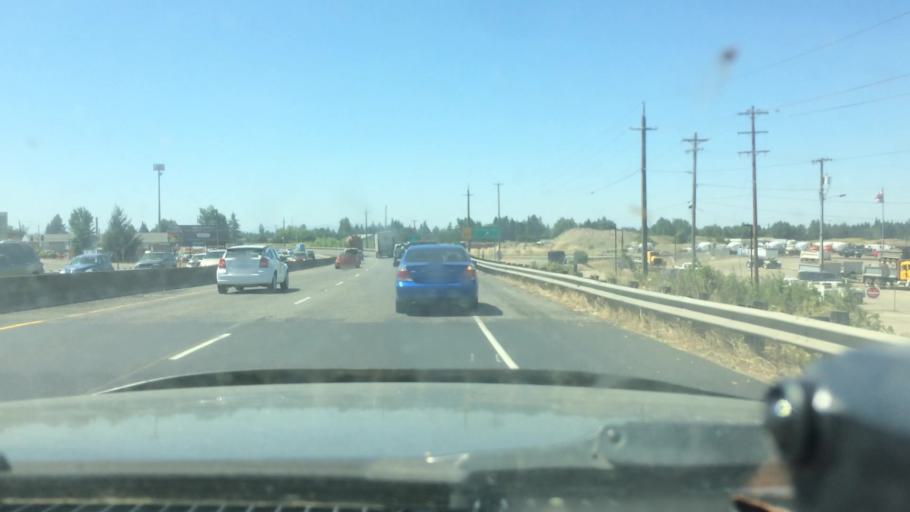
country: US
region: Oregon
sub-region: Lane County
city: Eugene
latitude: 44.0961
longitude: -123.1082
